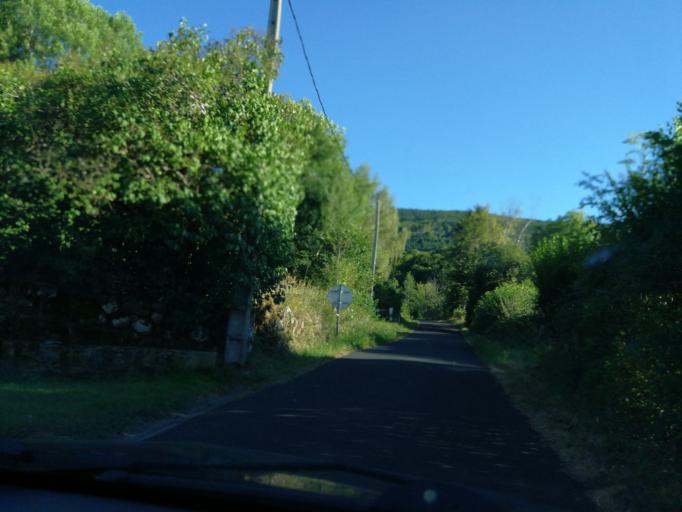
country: FR
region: Auvergne
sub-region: Departement du Cantal
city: Vic-sur-Cere
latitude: 45.0850
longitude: 2.5669
